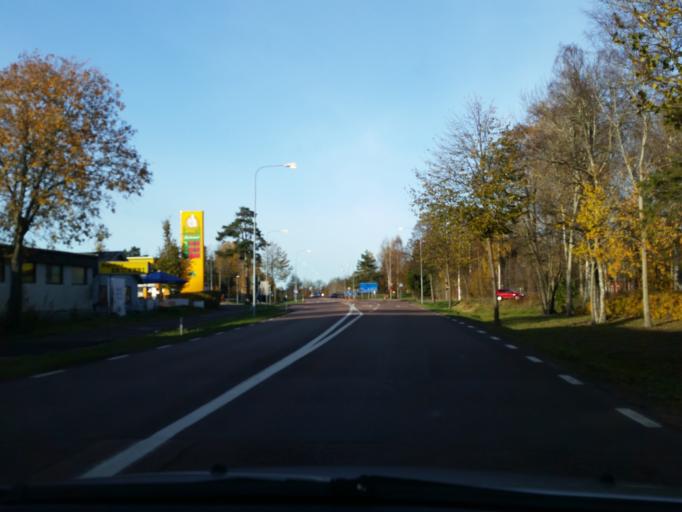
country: AX
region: Mariehamns stad
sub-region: Mariehamn
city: Mariehamn
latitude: 60.1105
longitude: 19.9303
